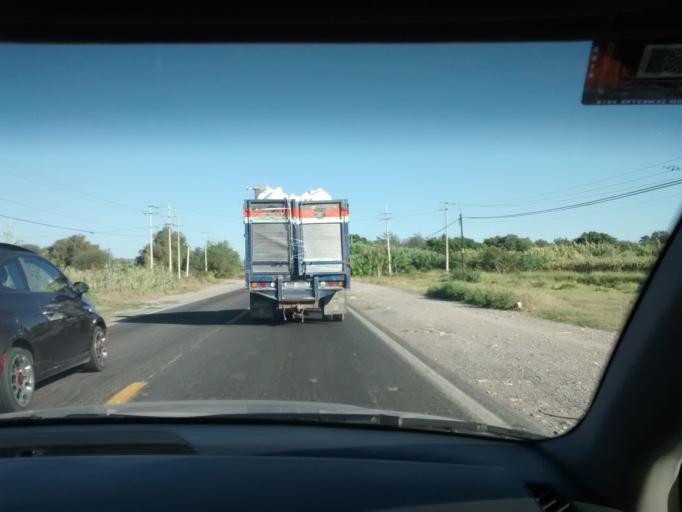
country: MX
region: Puebla
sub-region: Tehuacan
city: Magdalena Cuayucatepec
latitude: 18.5280
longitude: -97.5177
